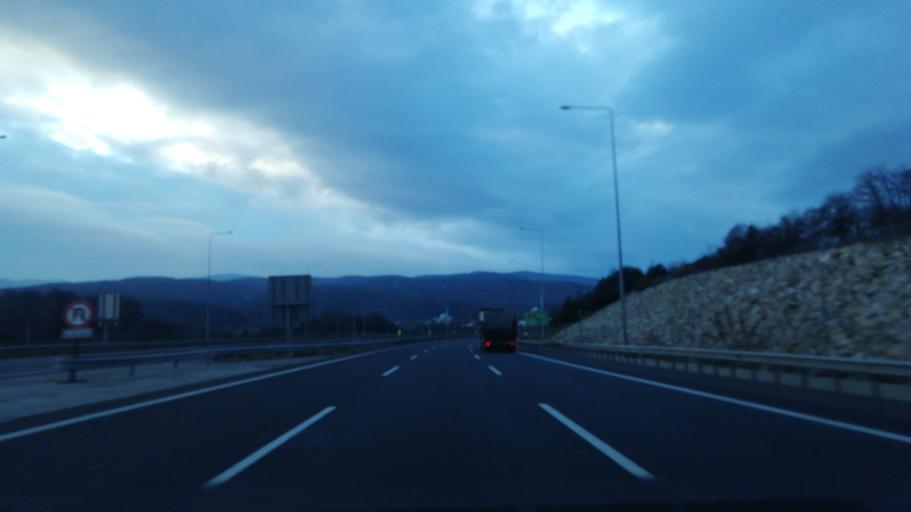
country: TR
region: Duzce
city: Kaynasli
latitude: 40.7243
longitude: 31.4553
